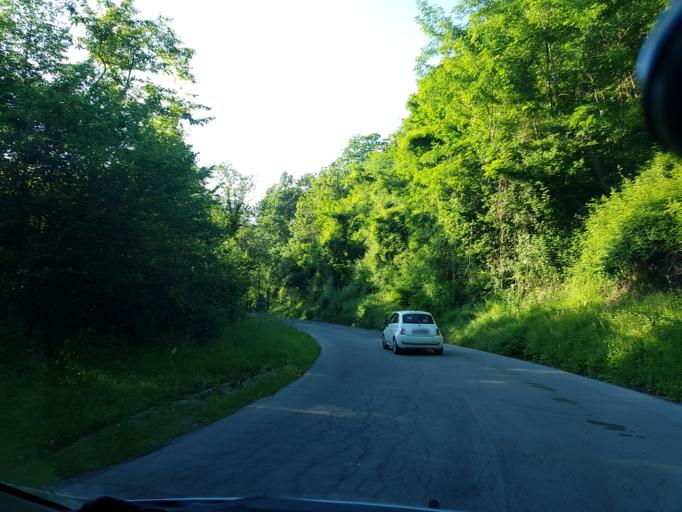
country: IT
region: Tuscany
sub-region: Provincia di Lucca
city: Minucciano
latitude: 44.1784
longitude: 10.2023
